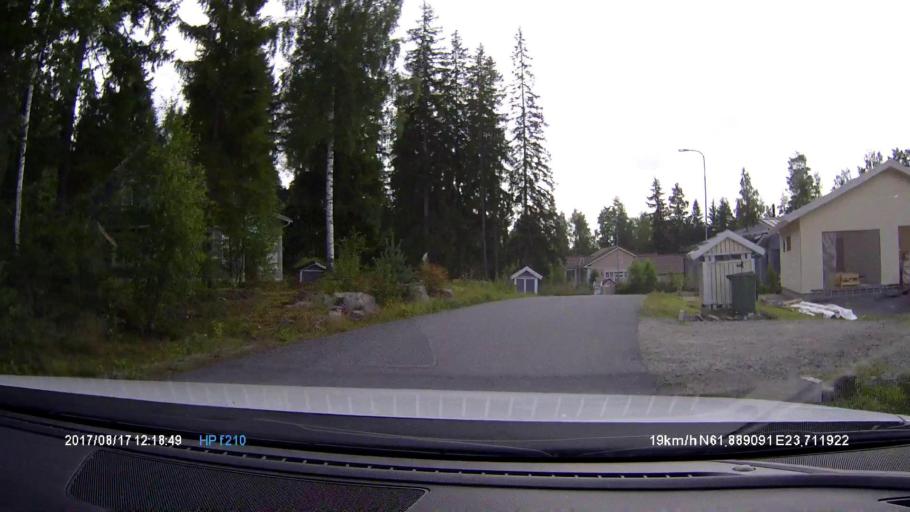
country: FI
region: Pirkanmaa
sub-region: Tampere
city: Kuru
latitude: 61.8888
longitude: 23.7125
